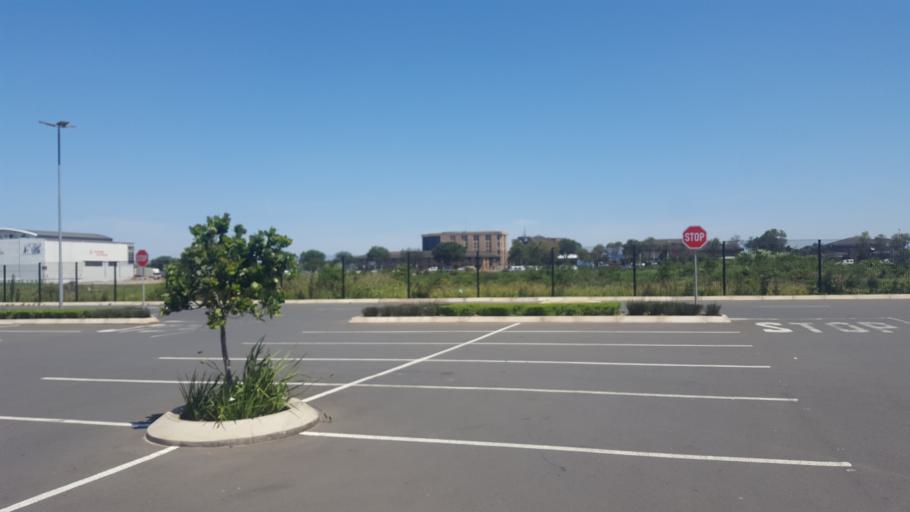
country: ZA
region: KwaZulu-Natal
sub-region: uThungulu District Municipality
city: Richards Bay
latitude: -28.7476
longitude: 32.0506
